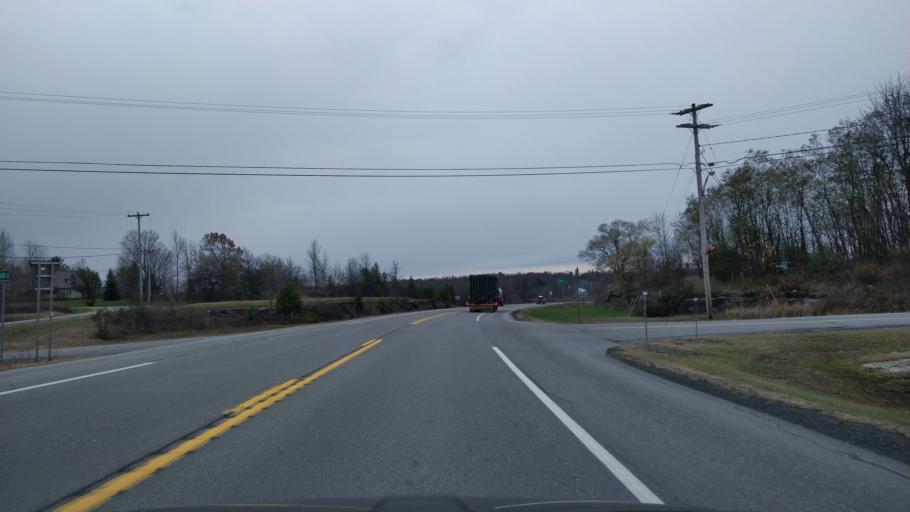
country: CA
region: Ontario
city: Brockville
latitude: 44.5837
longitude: -75.6389
